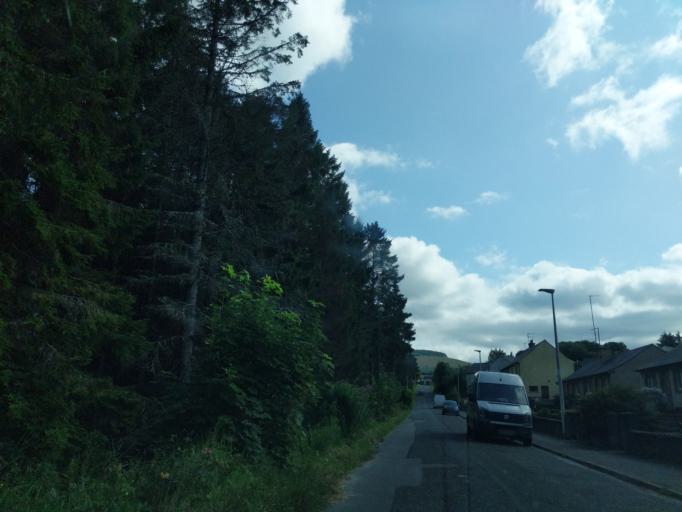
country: GB
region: Scotland
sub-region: Moray
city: Rothes
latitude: 57.4898
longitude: -3.1832
